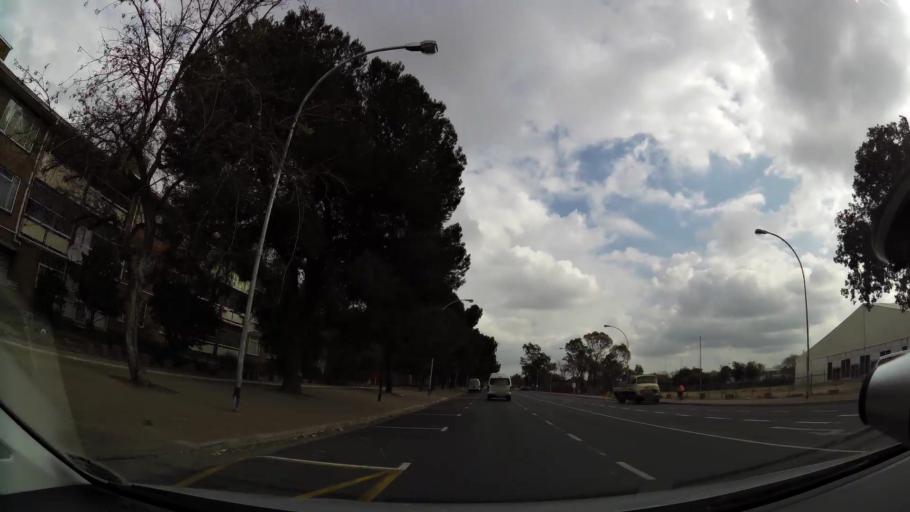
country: ZA
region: Orange Free State
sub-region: Mangaung Metropolitan Municipality
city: Bloemfontein
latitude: -29.1194
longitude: 26.2035
